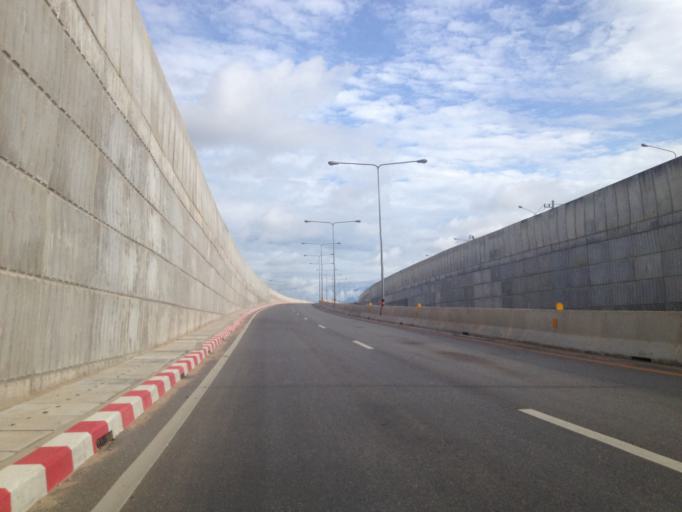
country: TH
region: Chiang Mai
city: Mae Wang
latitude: 18.6068
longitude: 98.8350
